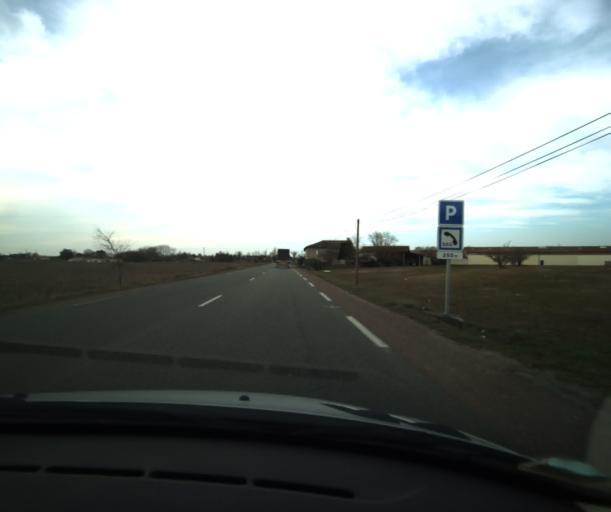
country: FR
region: Midi-Pyrenees
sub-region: Departement du Tarn-et-Garonne
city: Saint-Porquier
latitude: 43.9946
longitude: 1.1885
